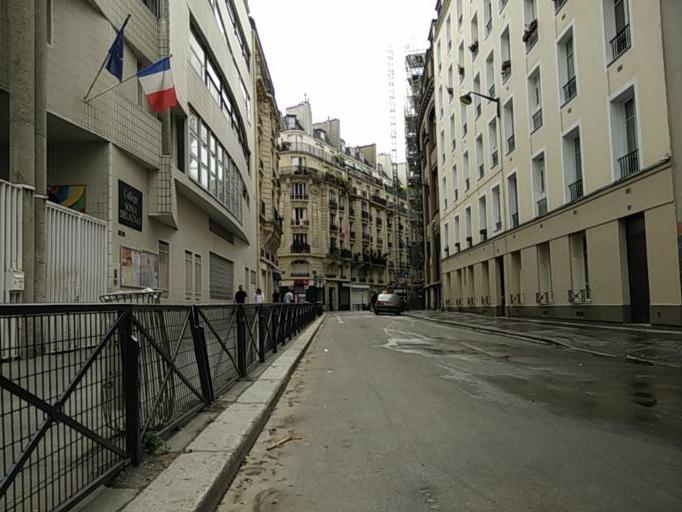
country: FR
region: Ile-de-France
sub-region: Departement de Seine-Saint-Denis
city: Le Pre-Saint-Gervais
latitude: 48.8860
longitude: 2.3777
